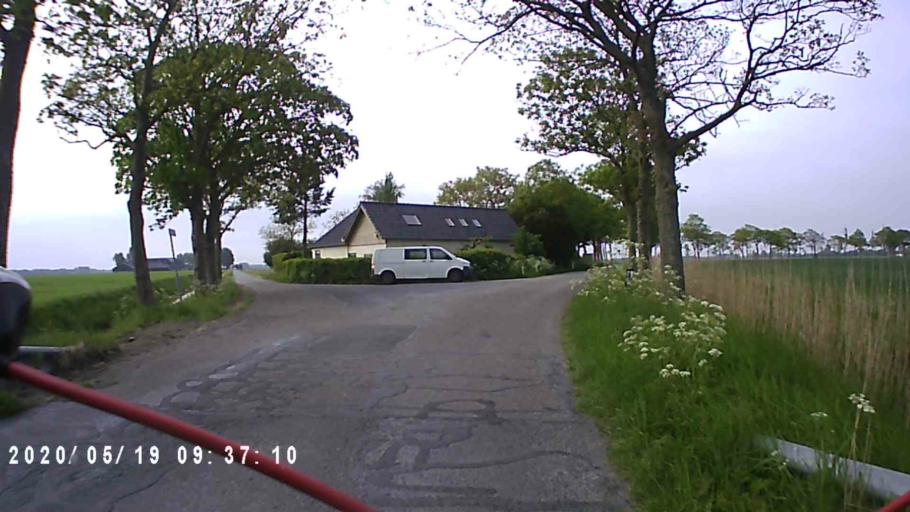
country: NL
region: Groningen
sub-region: Gemeente Zuidhorn
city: Grijpskerk
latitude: 53.2909
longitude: 6.2841
